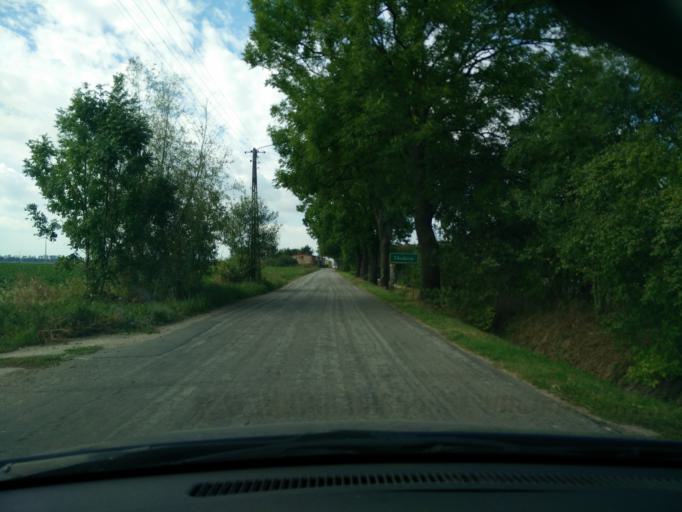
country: PL
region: Greater Poland Voivodeship
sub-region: Powiat sredzki
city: Dominowo
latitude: 52.2271
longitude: 17.3701
